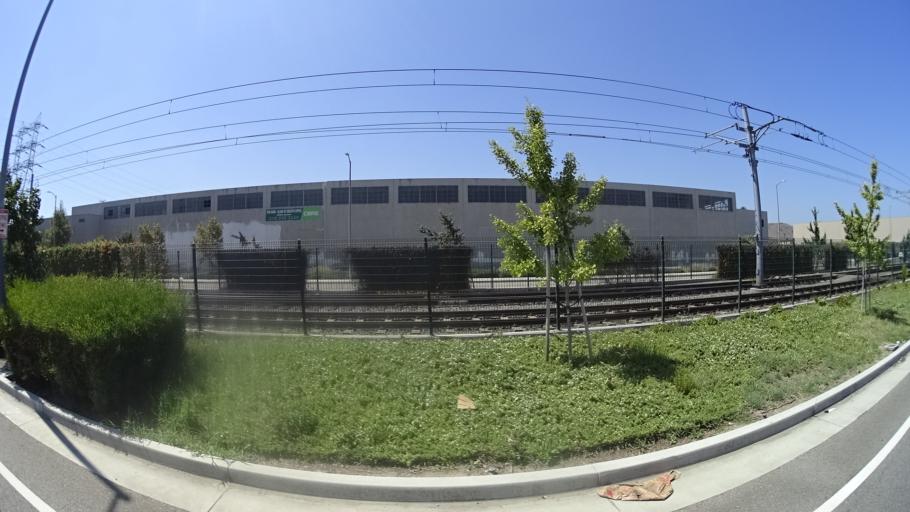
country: US
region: California
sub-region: Los Angeles County
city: Culver City
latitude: 34.0262
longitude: -118.3675
